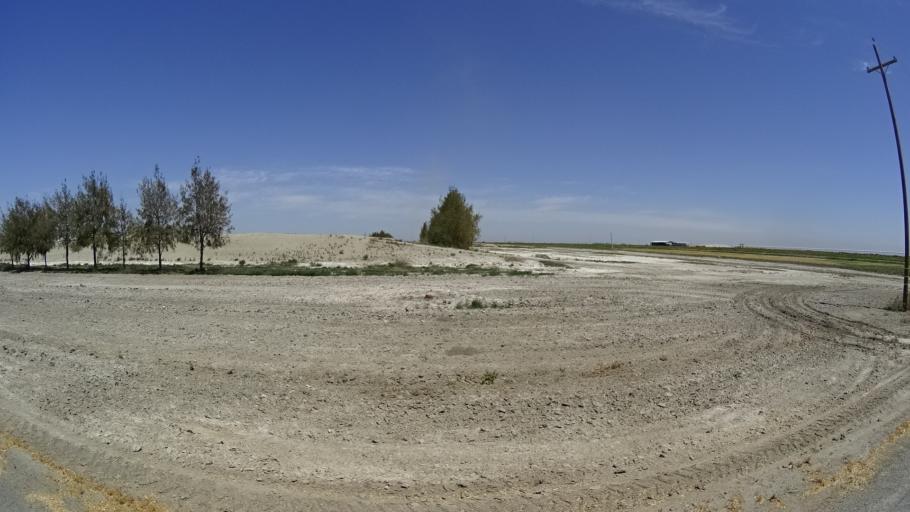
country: US
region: California
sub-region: Kings County
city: Stratford
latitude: 36.1526
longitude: -119.7375
